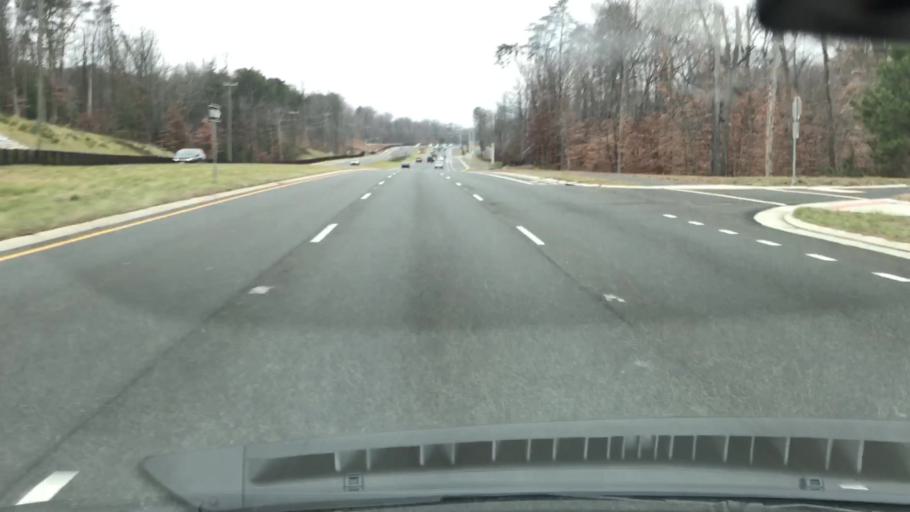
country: US
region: Virginia
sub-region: Fairfax County
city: Newington
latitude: 38.7076
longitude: -77.1780
